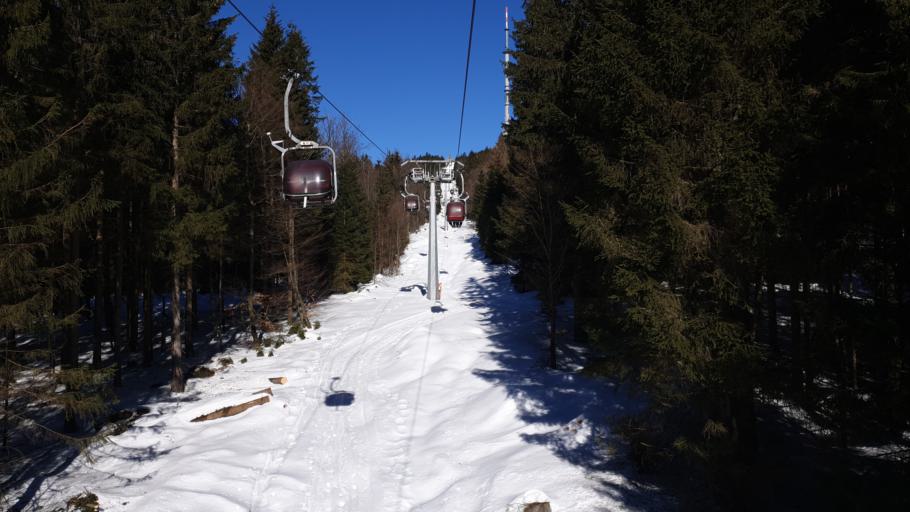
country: DE
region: Bavaria
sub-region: Upper Franconia
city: Bischofsgrun
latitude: 50.0221
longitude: 11.8081
